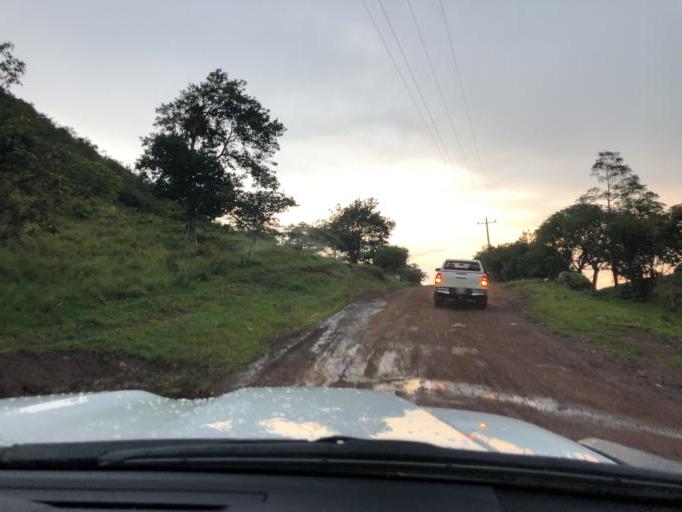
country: NI
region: Chontales
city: La Libertad
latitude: 12.1735
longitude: -85.1771
